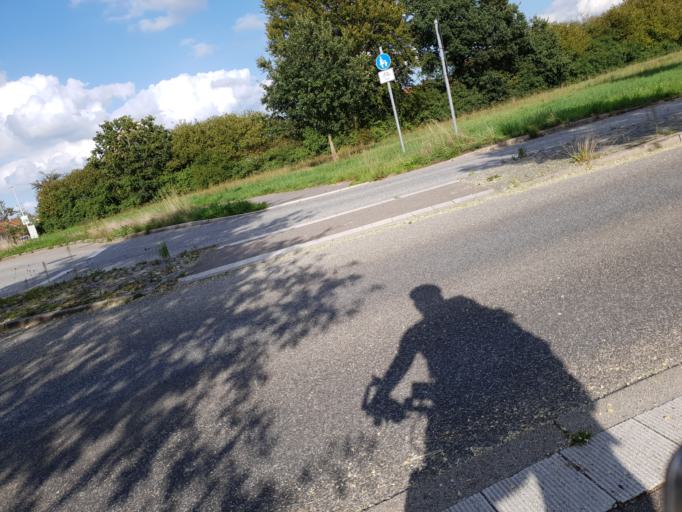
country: DE
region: Schleswig-Holstein
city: Kronshagen
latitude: 54.3508
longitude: 10.0713
